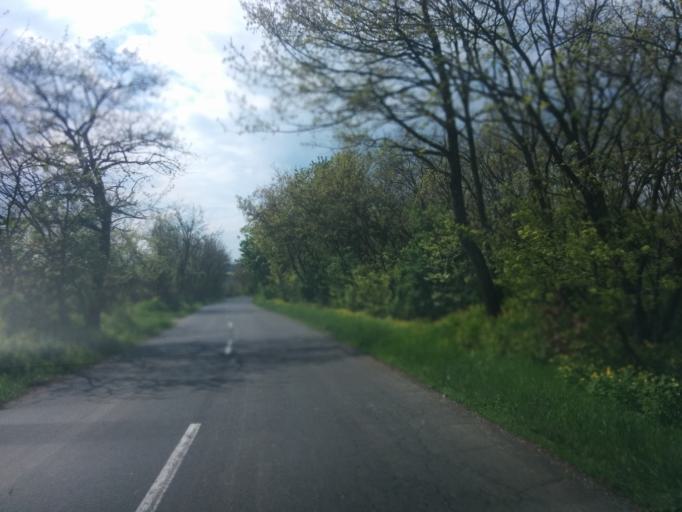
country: HU
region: Pest
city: Acsa
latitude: 47.8444
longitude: 19.3217
